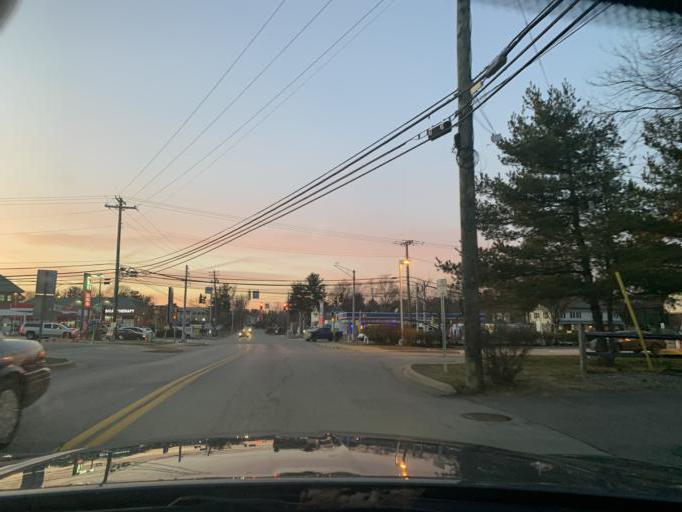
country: US
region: Maryland
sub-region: Anne Arundel County
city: Glen Burnie
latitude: 39.1483
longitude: -76.6378
